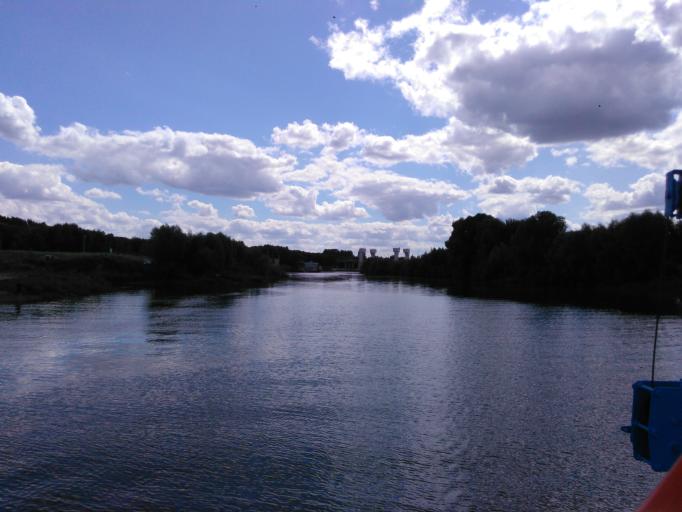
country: RU
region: Rjazan
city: Ryazan'
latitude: 54.6499
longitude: 39.7648
